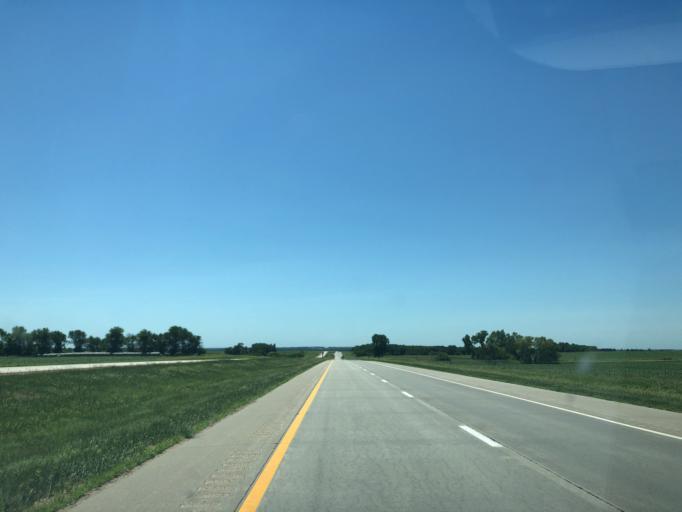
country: US
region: Kansas
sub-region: Cloud County
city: Concordia
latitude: 39.6485
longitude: -97.6604
